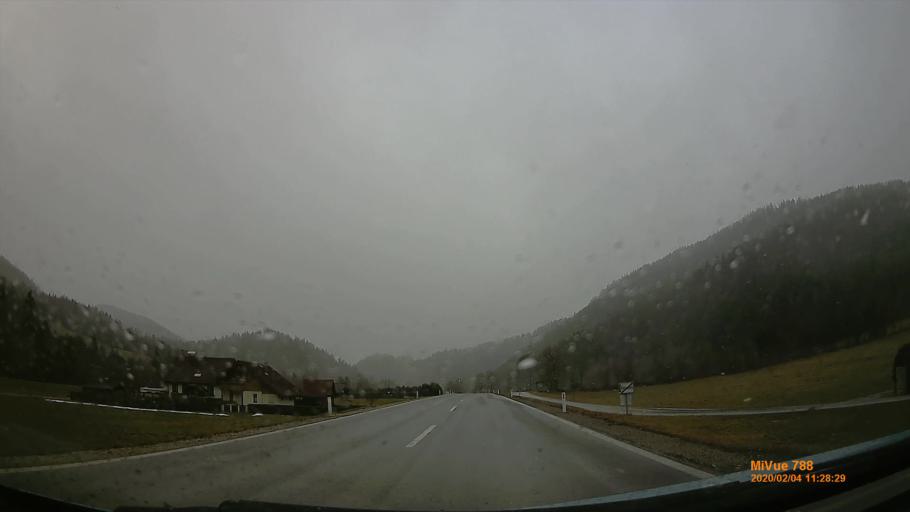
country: AT
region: Styria
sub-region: Politischer Bezirk Bruck-Muerzzuschlag
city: Kapellen
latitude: 47.6480
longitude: 15.6264
